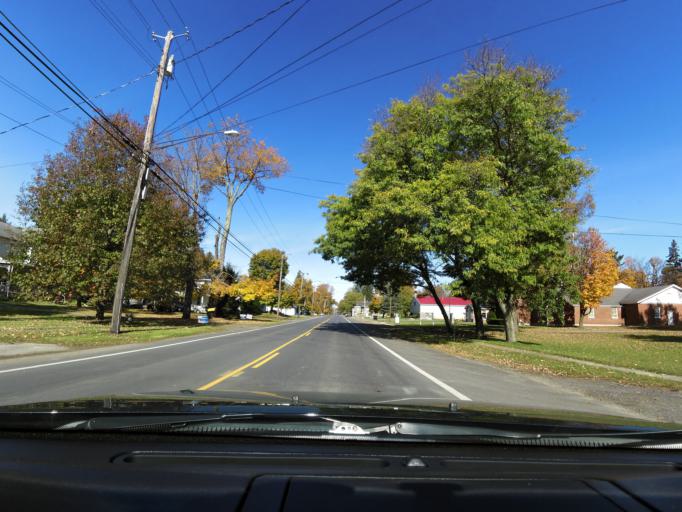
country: US
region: New York
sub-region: Wyoming County
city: Castile
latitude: 42.6397
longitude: -78.1341
